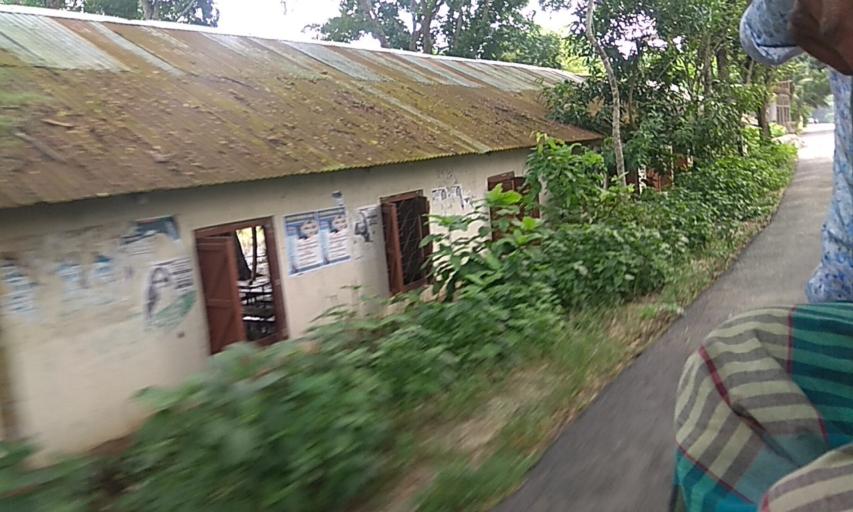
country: BD
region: Dhaka
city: Dohar
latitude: 23.4754
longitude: 90.0513
